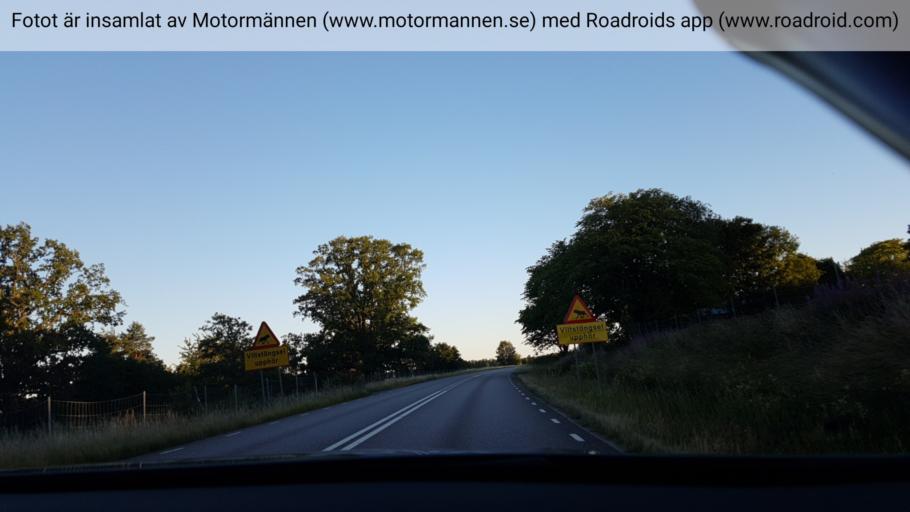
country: SE
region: Vaestra Goetaland
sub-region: Hjo Kommun
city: Hjo
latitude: 58.3332
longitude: 14.3348
